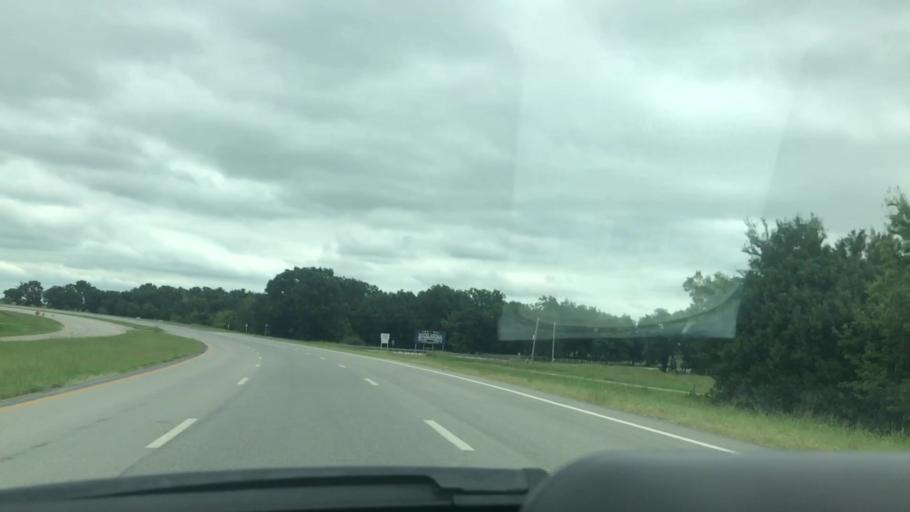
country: US
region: Oklahoma
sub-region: Mayes County
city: Pryor
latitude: 36.3640
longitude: -95.2923
